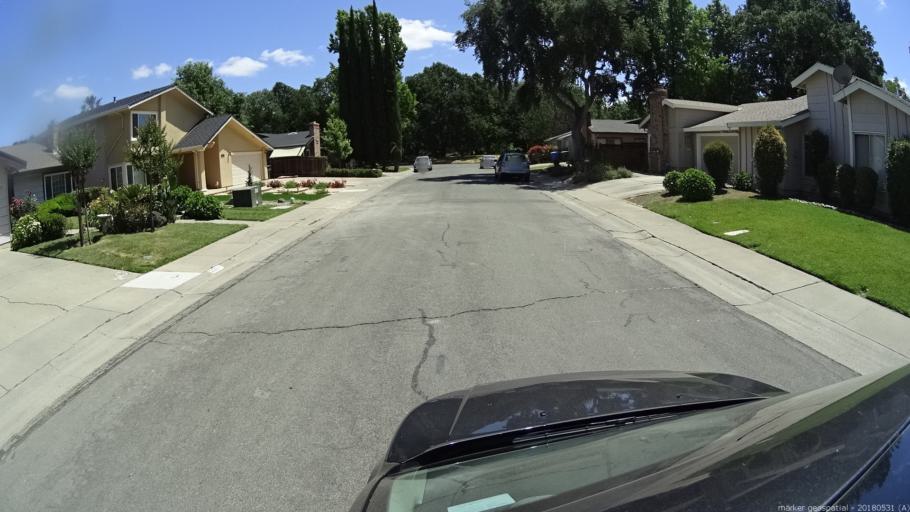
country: US
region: California
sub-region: Sacramento County
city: Sacramento
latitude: 38.6180
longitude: -121.5065
